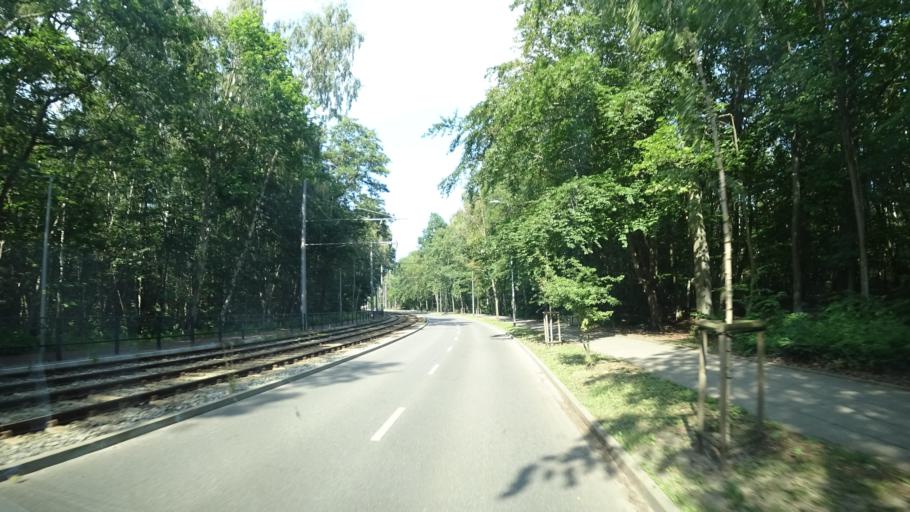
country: PL
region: Pomeranian Voivodeship
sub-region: Gdansk
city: Gdansk
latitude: 54.3661
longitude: 18.7232
